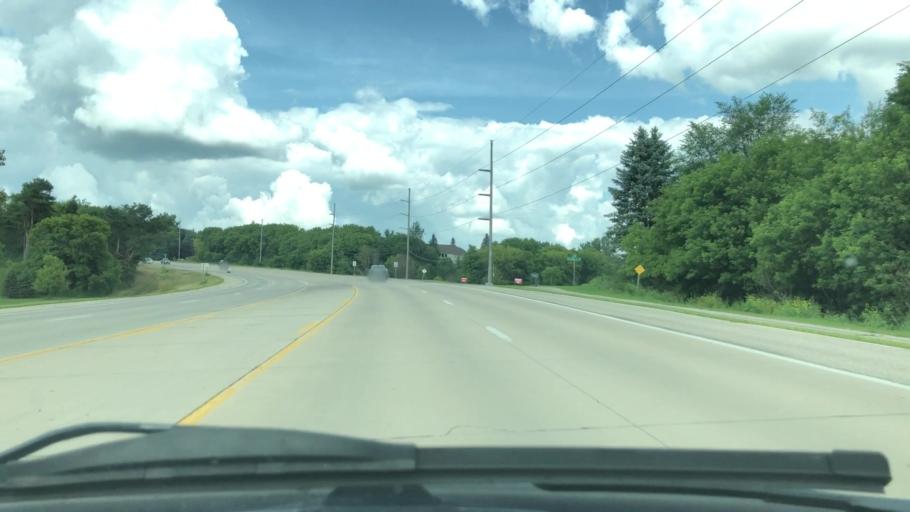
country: US
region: Minnesota
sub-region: Olmsted County
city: Rochester
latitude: 44.0080
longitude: -92.5086
